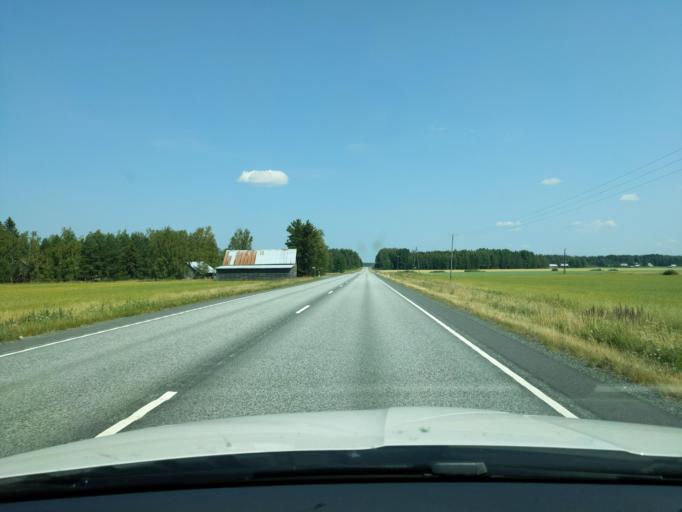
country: FI
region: Haeme
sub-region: Forssa
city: Ypaejae
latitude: 60.7469
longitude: 23.2857
